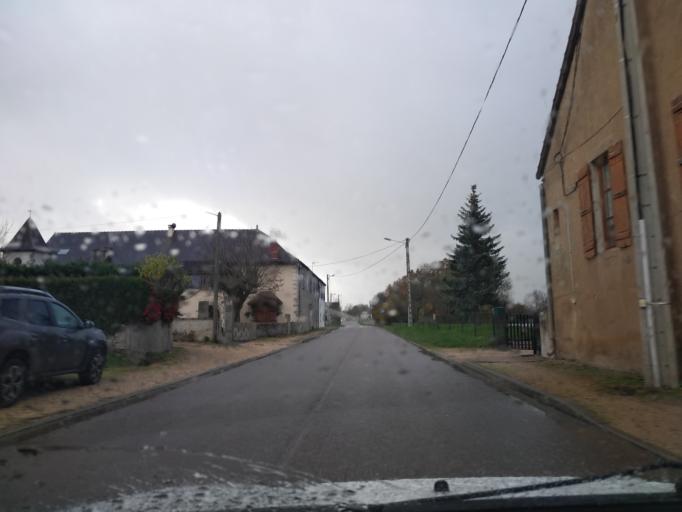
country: FR
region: Bourgogne
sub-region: Departement de Saone-et-Loire
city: Saint-Leger-sur-Dheune
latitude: 46.8765
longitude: 4.6605
